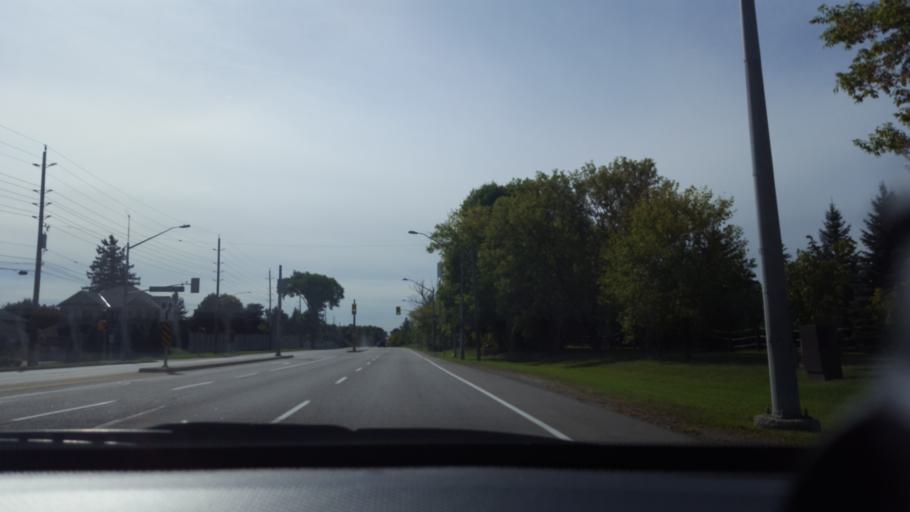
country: CA
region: Ontario
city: Newmarket
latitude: 43.9898
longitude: -79.4933
